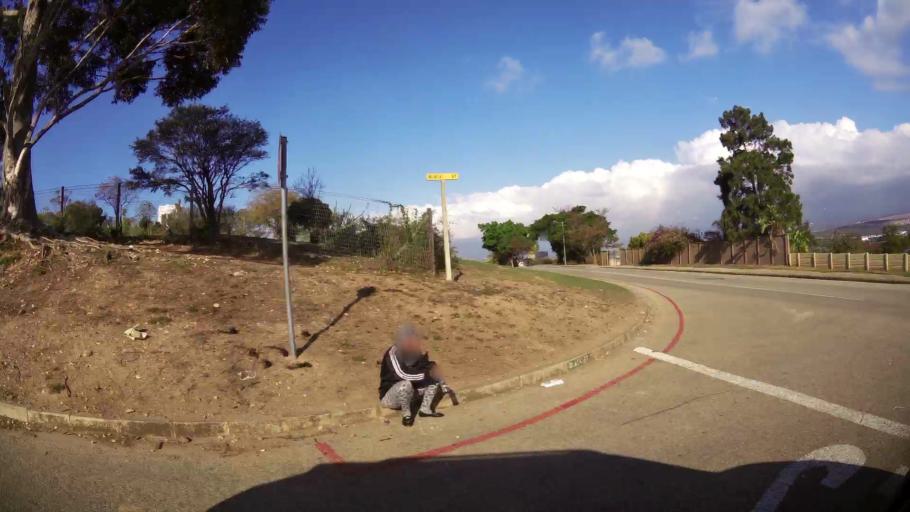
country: ZA
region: Eastern Cape
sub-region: Nelson Mandela Bay Metropolitan Municipality
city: Uitenhage
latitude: -33.7670
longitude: 25.4051
